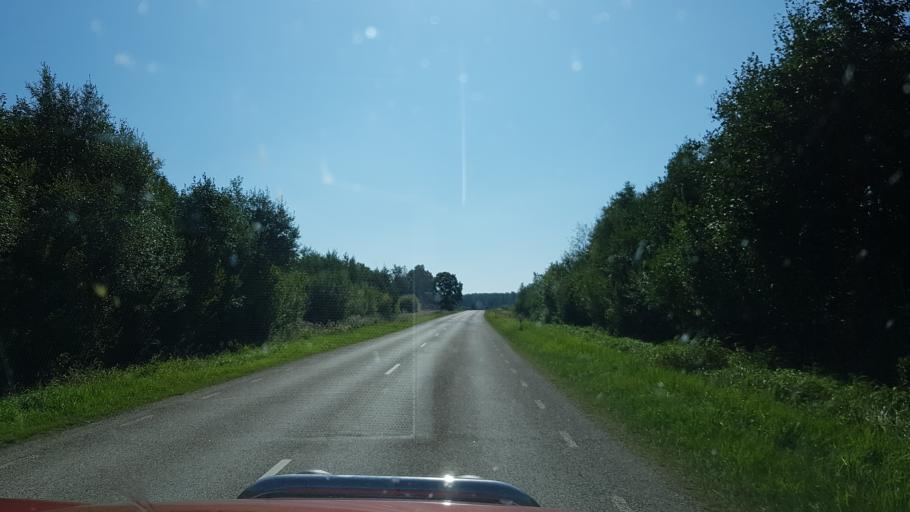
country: EE
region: Polvamaa
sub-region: Polva linn
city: Polva
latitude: 58.2594
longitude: 27.1794
